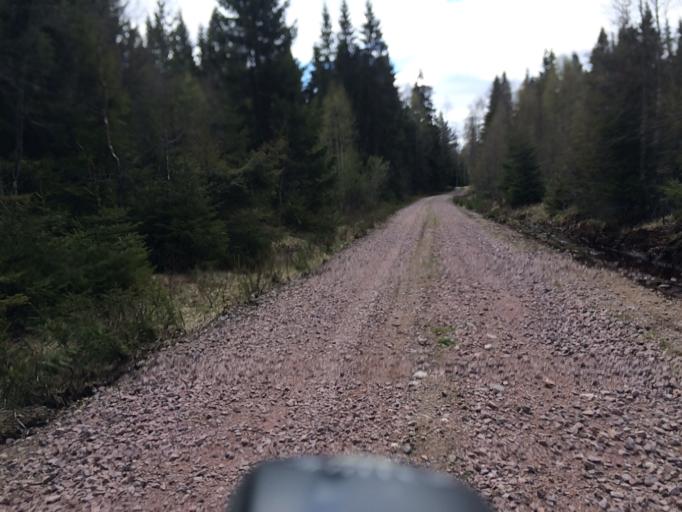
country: SE
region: OErebro
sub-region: Hallefors Kommun
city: Haellefors
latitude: 60.0451
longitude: 14.5154
